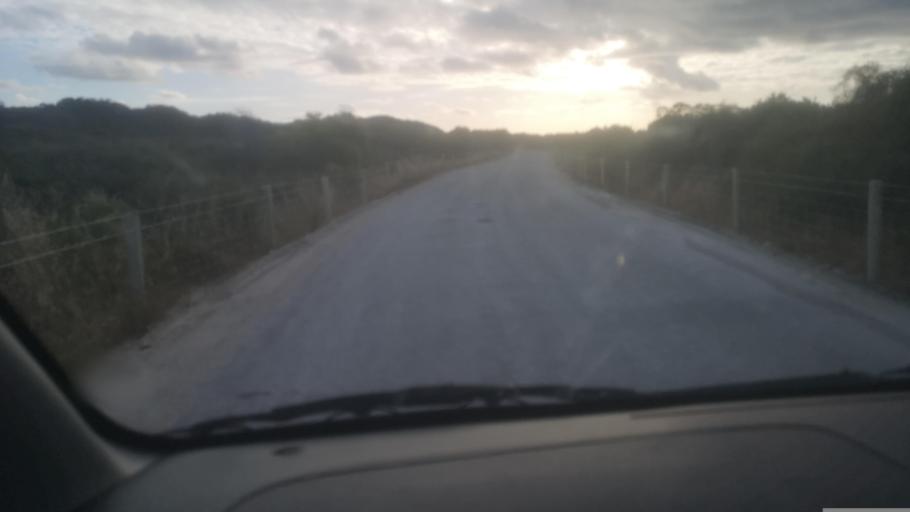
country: AU
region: Western Australia
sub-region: Wanneroo
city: Two Rocks
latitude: -31.5187
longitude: 115.6110
